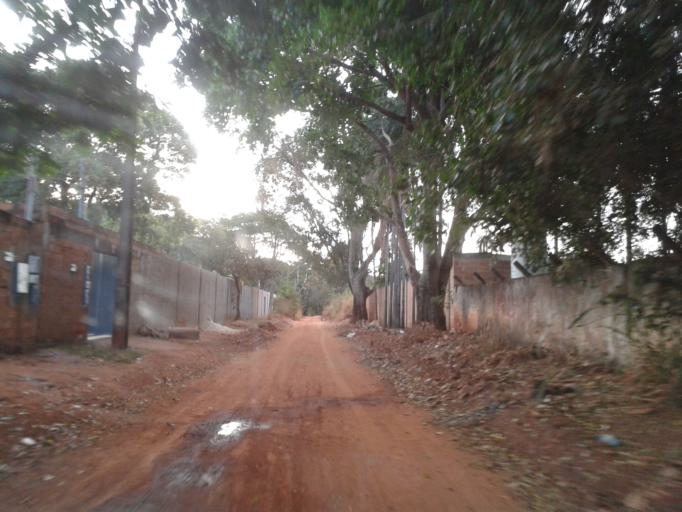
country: BR
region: Goias
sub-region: Goiania
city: Goiania
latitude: -16.6418
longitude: -49.3562
